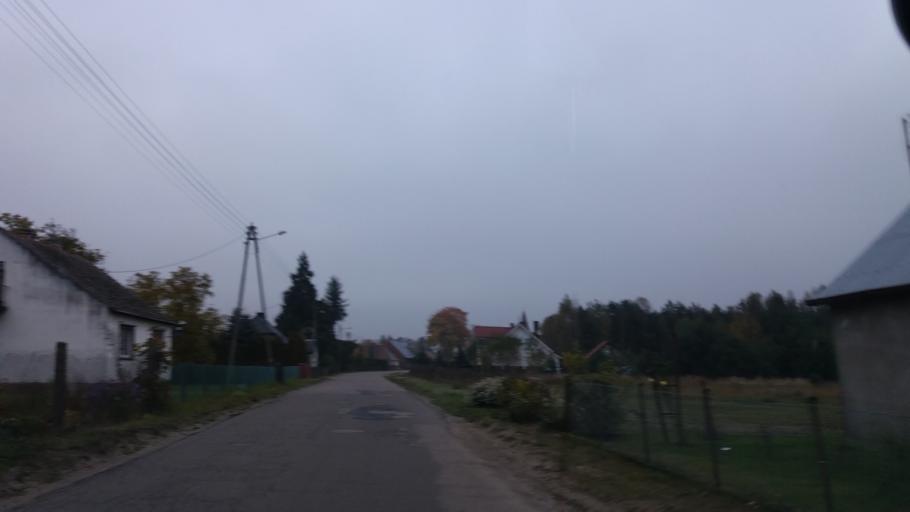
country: PL
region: Lubusz
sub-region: Powiat strzelecko-drezdenecki
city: Dobiegniew
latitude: 53.0748
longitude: 15.7783
